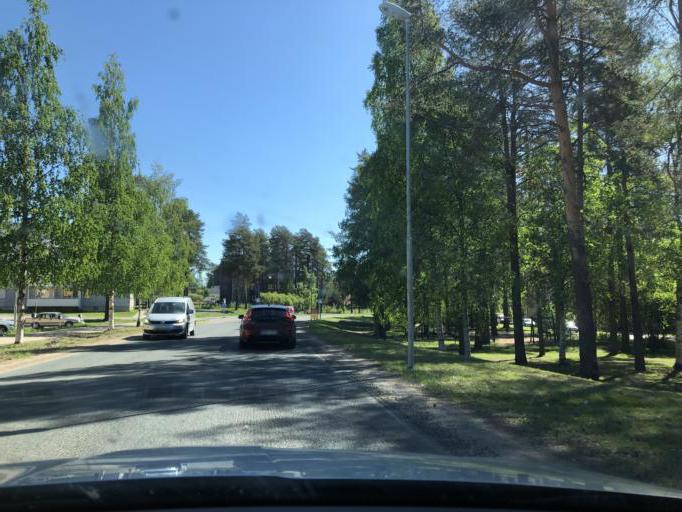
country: SE
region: Norrbotten
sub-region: Kalix Kommun
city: Kalix
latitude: 65.8558
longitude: 23.1479
